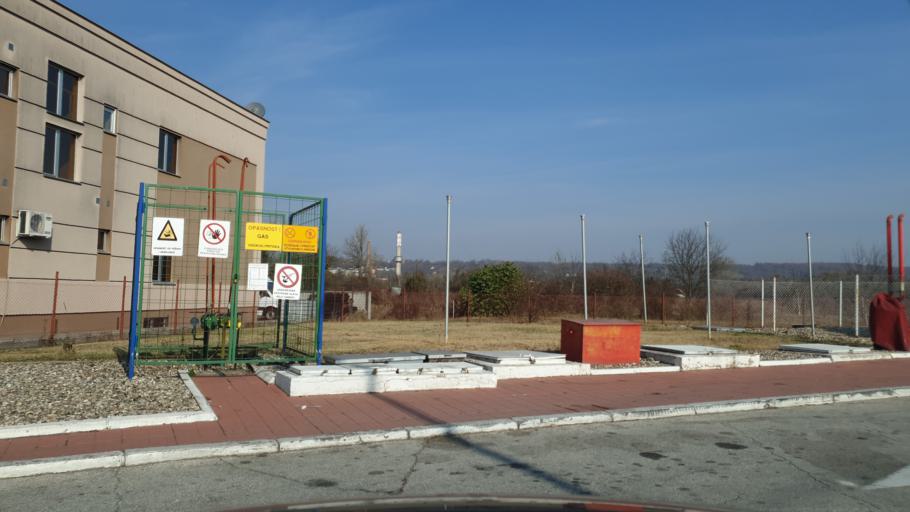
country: RS
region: Central Serbia
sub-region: Pomoravski Okrug
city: Paracin
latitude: 43.8585
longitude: 21.4300
